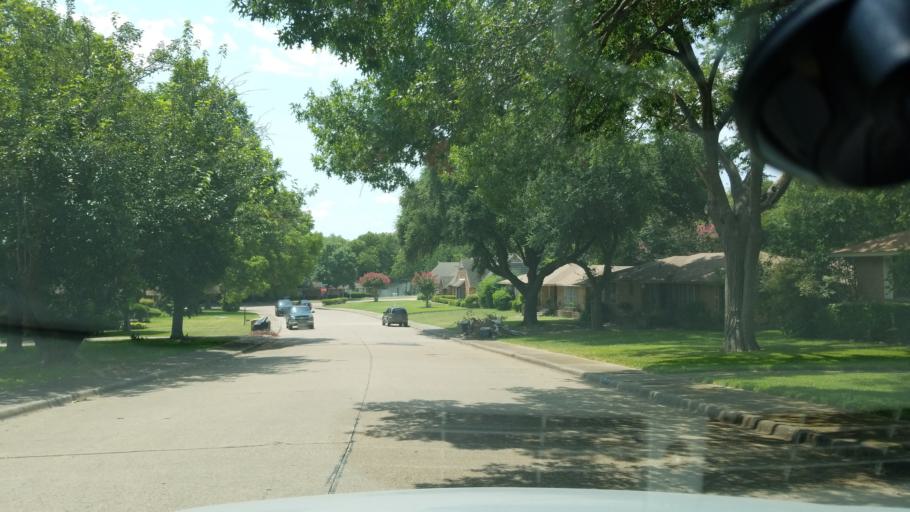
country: US
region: Texas
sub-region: Dallas County
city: Cockrell Hill
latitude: 32.6787
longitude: -96.8358
